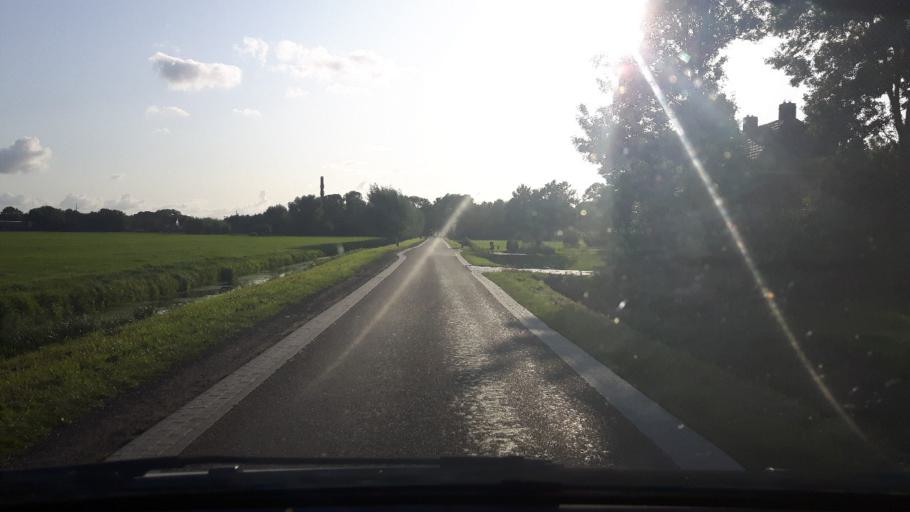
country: NL
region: Gelderland
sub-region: Gemeente Hattem
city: Hattem
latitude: 52.5416
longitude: 6.0186
